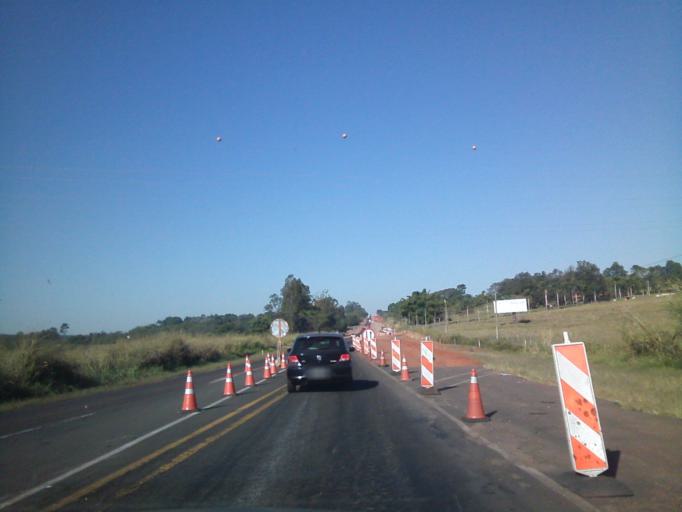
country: BR
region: Sao Paulo
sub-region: Pirapozinho
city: Pirapozinho
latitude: -22.2141
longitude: -51.4374
